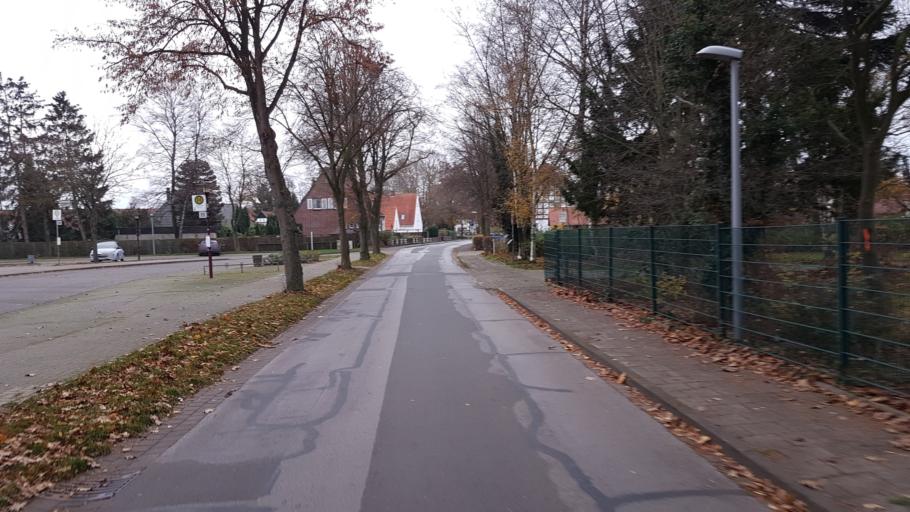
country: DE
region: North Rhine-Westphalia
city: Rahden
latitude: 52.4361
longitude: 8.6165
